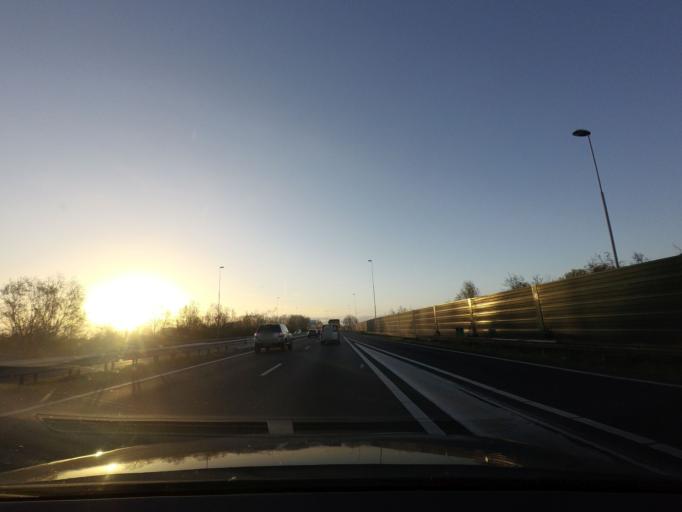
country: NL
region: North Holland
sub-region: Gemeente Zaanstad
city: Zaanstad
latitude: 52.4655
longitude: 4.8011
